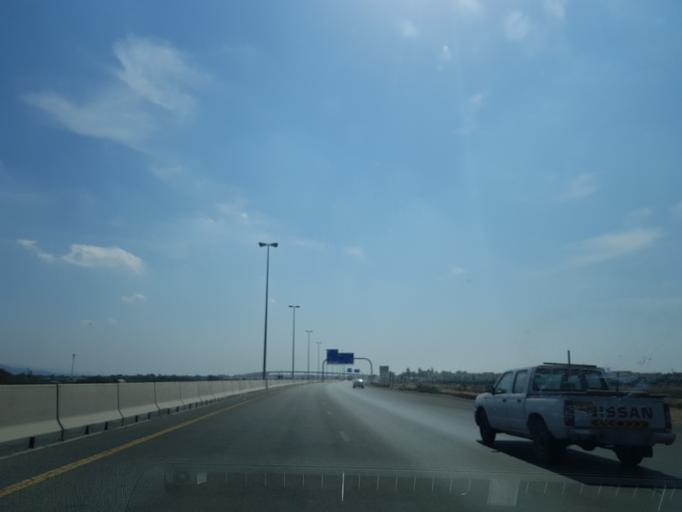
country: AE
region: Ra's al Khaymah
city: Ras al-Khaimah
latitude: 25.8444
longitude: 56.0191
